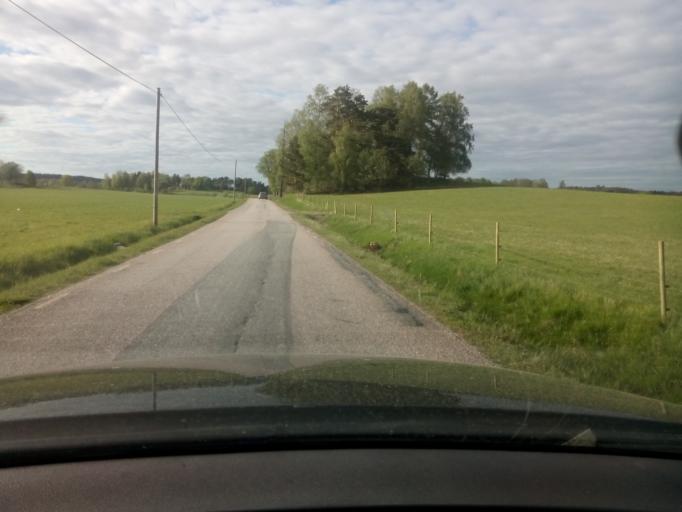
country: SE
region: Soedermanland
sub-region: Nykopings Kommun
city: Stigtomta
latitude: 58.9158
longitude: 16.8798
